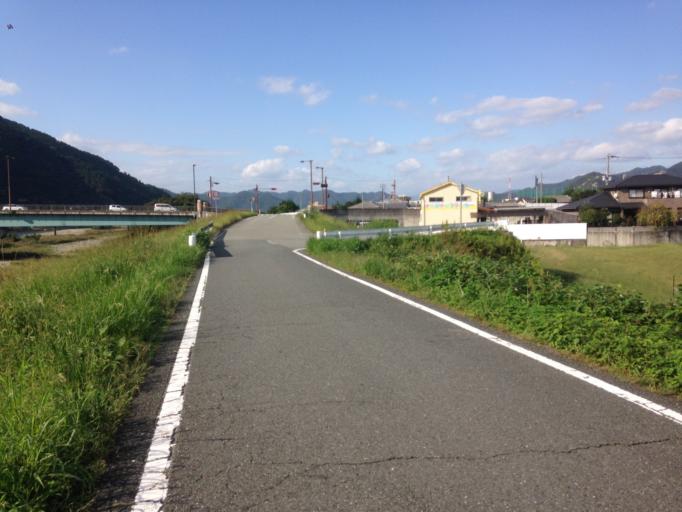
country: JP
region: Hyogo
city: Tatsunocho-tominaga
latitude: 34.8738
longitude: 134.5515
